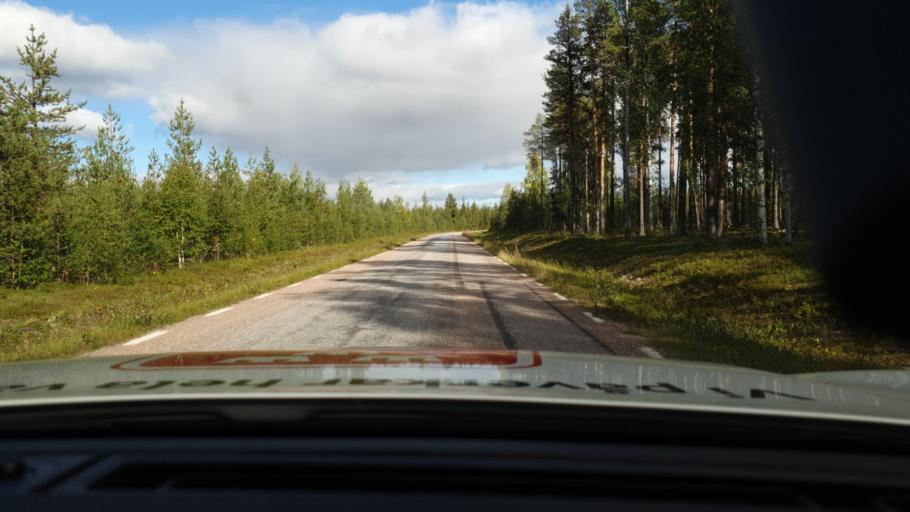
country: SE
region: Norrbotten
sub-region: Pajala Kommun
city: Pajala
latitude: 67.2526
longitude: 22.3366
